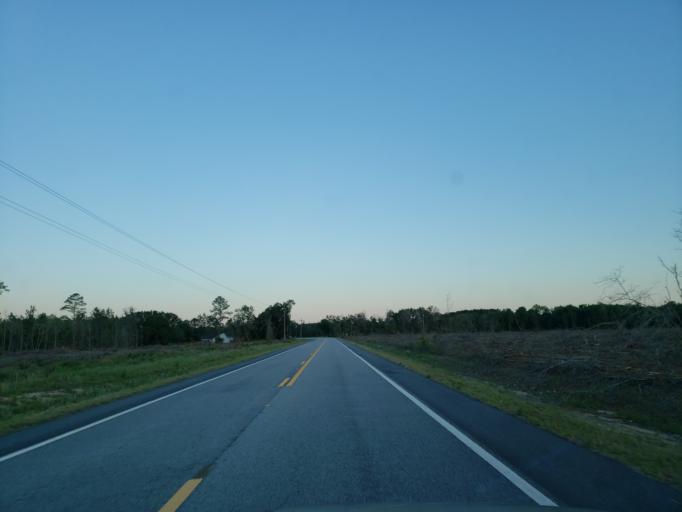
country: US
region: Georgia
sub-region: Echols County
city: Statenville
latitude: 30.5662
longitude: -83.1554
